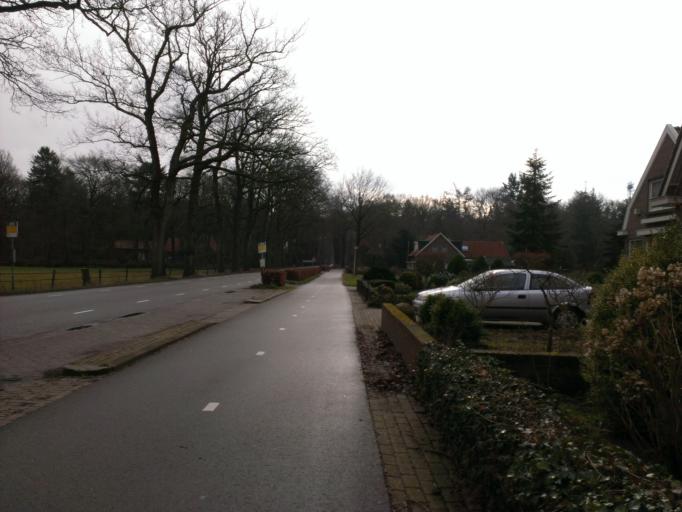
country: NL
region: Drenthe
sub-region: Gemeente Hoogeveen
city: Hoogeveen
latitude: 52.7482
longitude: 6.4678
